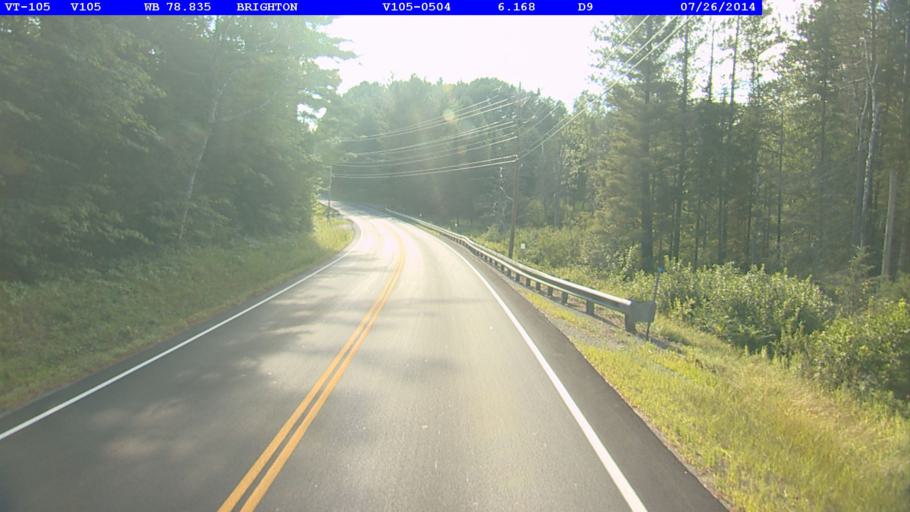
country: US
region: Vermont
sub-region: Caledonia County
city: Lyndonville
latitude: 44.8071
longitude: -71.8524
